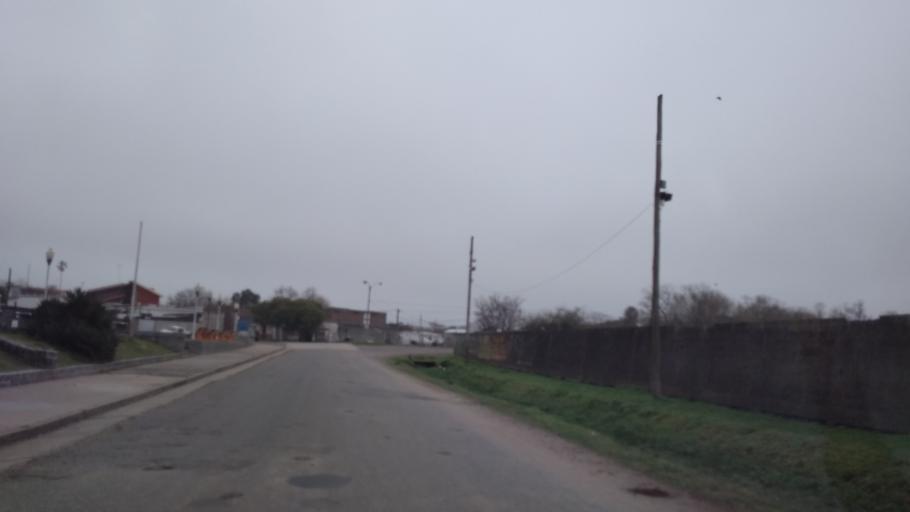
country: UY
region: Florida
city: Florida
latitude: -34.0923
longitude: -56.2080
